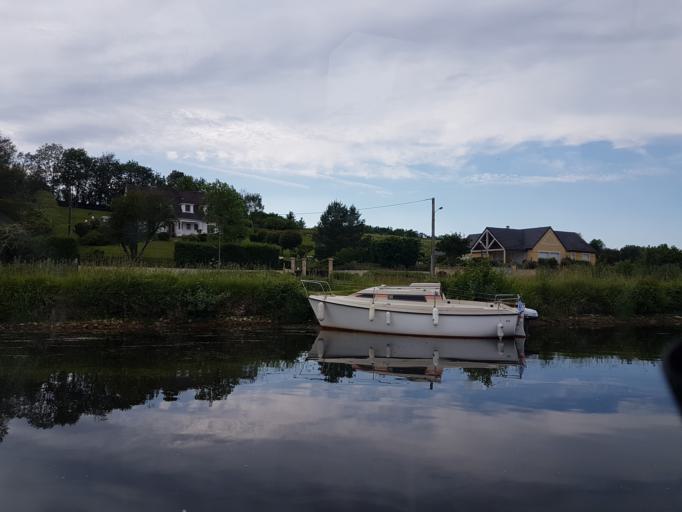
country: FR
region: Bourgogne
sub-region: Departement de l'Yonne
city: Moneteau
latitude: 47.8332
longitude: 3.5716
